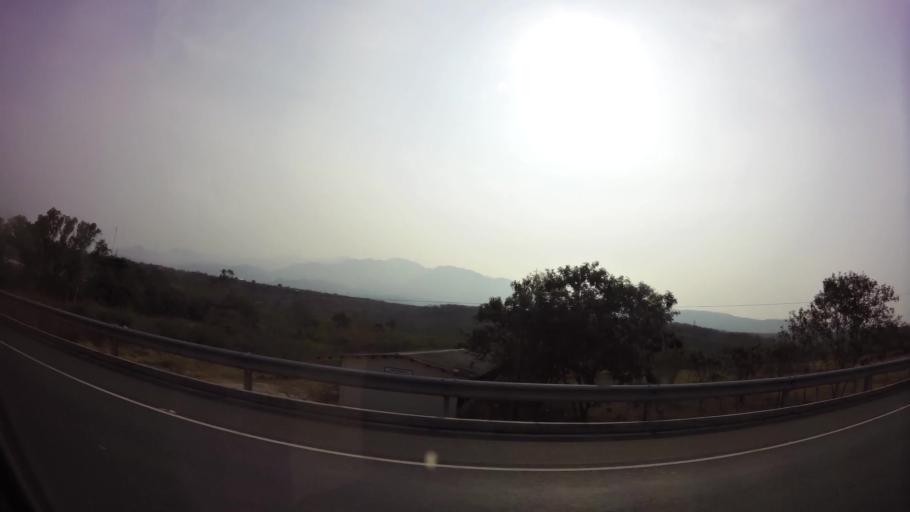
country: HN
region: Comayagua
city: Comayagua
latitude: 14.4119
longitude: -87.6230
